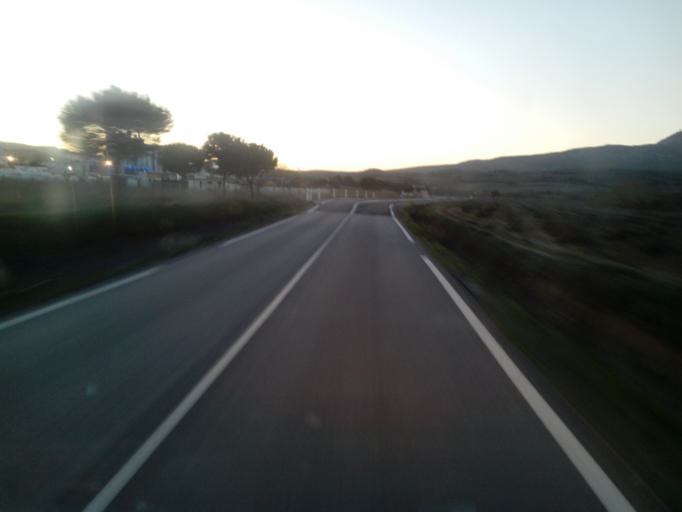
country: FR
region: Languedoc-Roussillon
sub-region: Departement des Pyrenees-Orientales
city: Baixas
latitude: 42.7807
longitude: 2.8054
